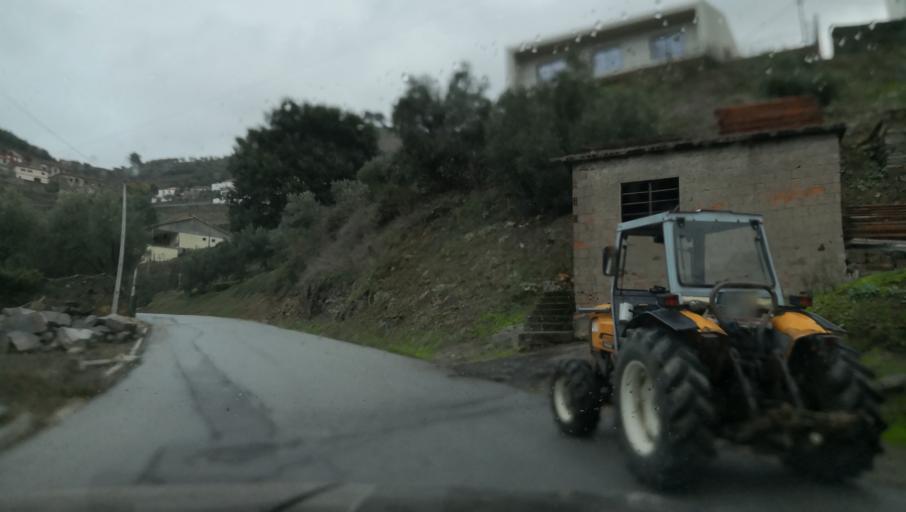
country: PT
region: Vila Real
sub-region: Santa Marta de Penaguiao
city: Santa Marta de Penaguiao
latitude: 41.2028
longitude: -7.7498
